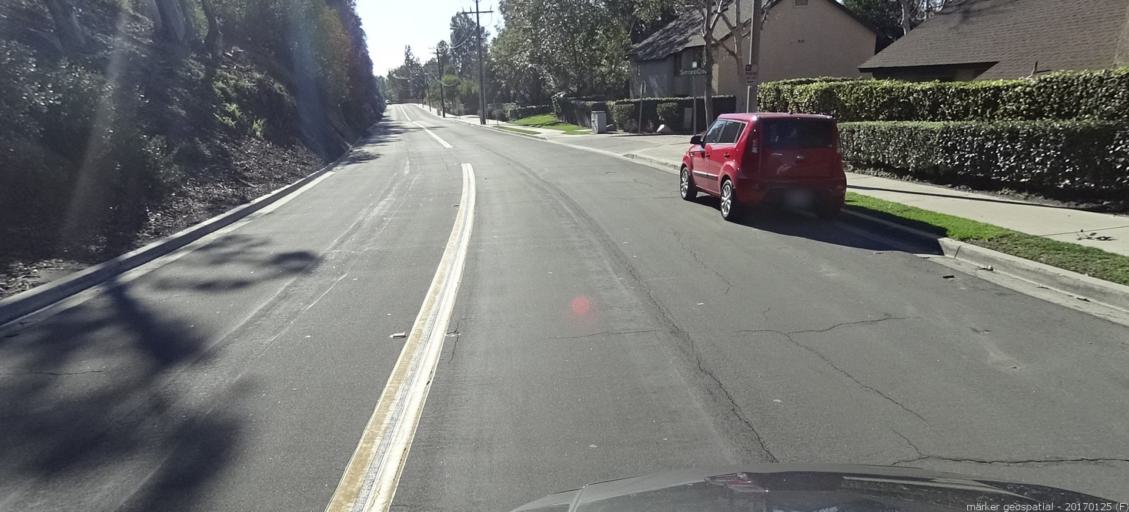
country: US
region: California
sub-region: Orange County
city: Lake Forest
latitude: 33.6585
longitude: -117.6745
